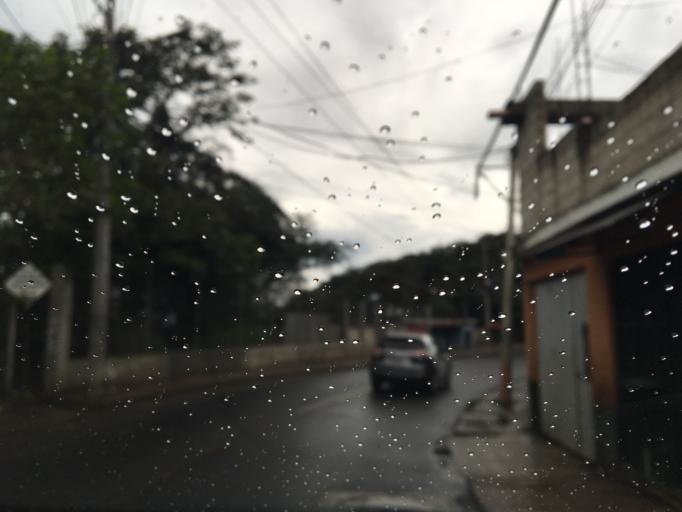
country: GT
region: Guatemala
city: Santa Catarina Pinula
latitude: 14.5457
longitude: -90.5124
